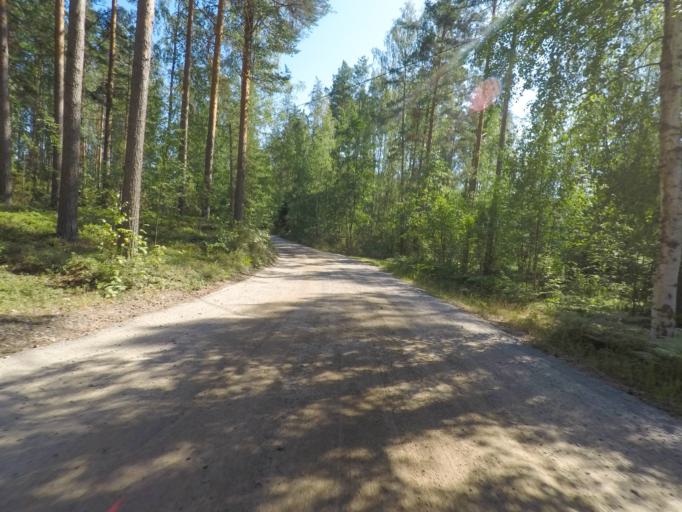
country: FI
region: Southern Savonia
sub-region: Mikkeli
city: Puumala
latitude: 61.4233
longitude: 28.0389
